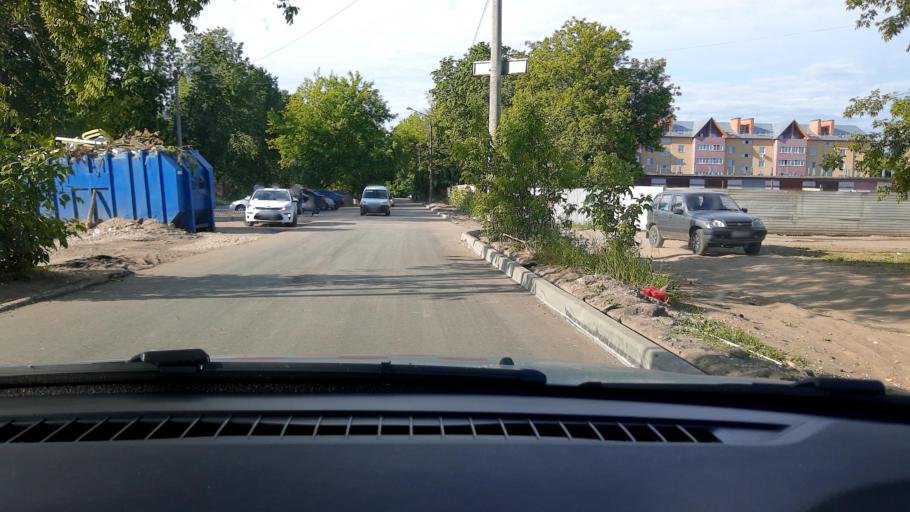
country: RU
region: Nizjnij Novgorod
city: Gorbatovka
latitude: 56.2500
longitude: 43.8323
